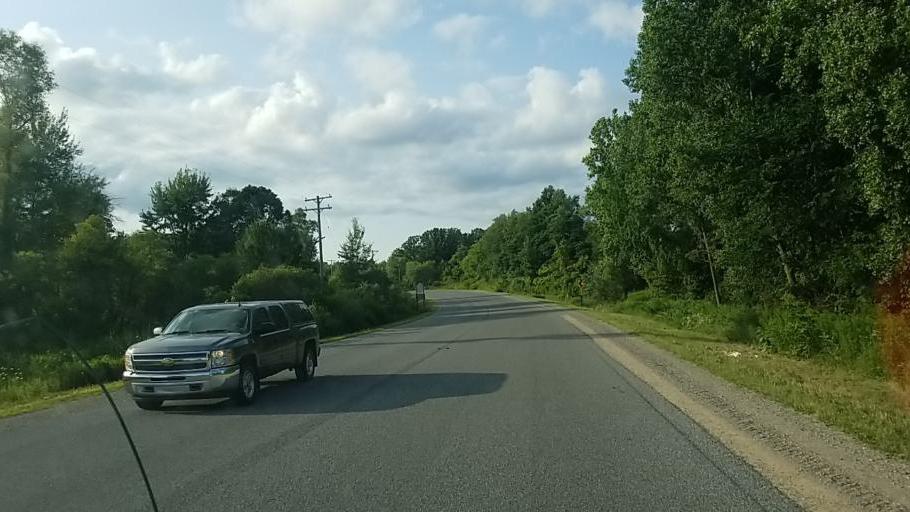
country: US
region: Michigan
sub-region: Kent County
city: Lowell
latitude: 43.0449
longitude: -85.3522
